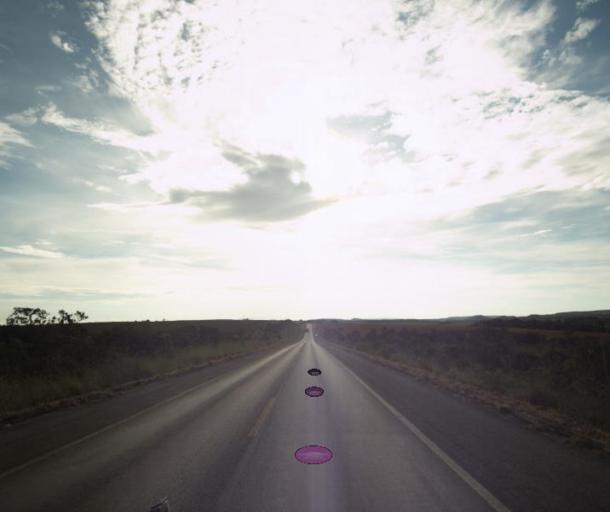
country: BR
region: Goias
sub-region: Pirenopolis
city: Pirenopolis
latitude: -15.7640
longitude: -48.7024
